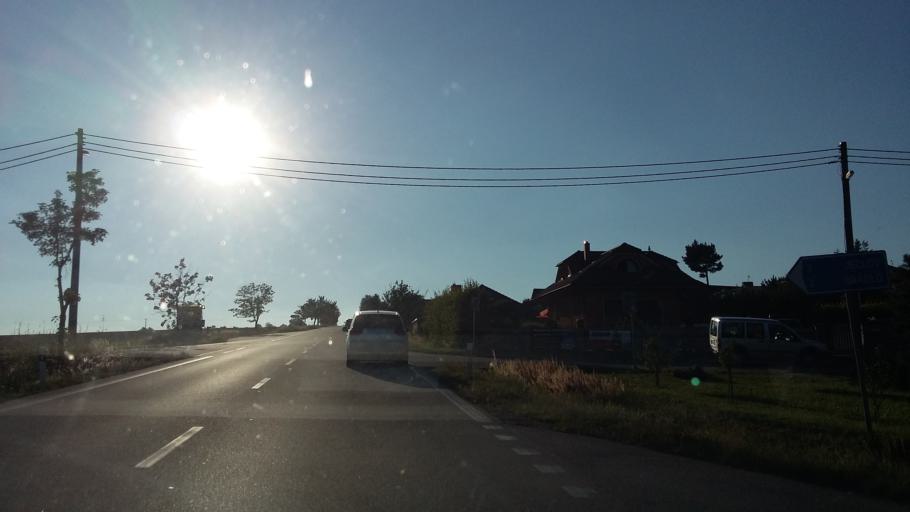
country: CZ
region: Vysocina
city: Velky Beranov
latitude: 49.4023
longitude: 15.6669
